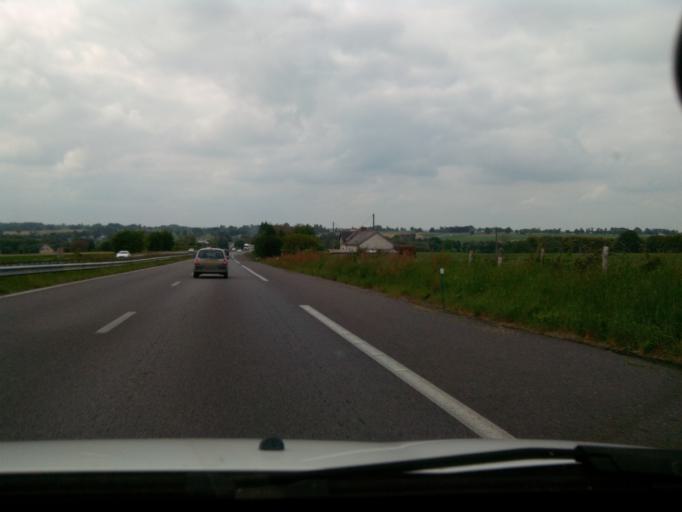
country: FR
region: Brittany
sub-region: Departement d'Ille-et-Vilaine
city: Quedillac
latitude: 48.2189
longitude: -2.1045
